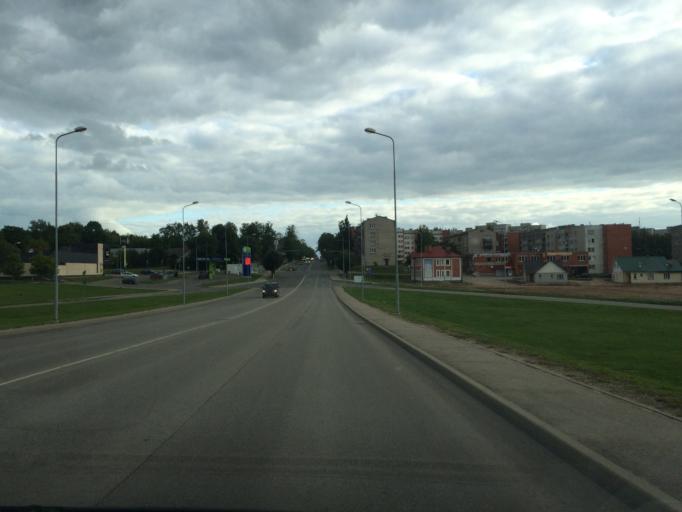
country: LV
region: Rezekne
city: Rezekne
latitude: 56.5179
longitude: 27.3377
